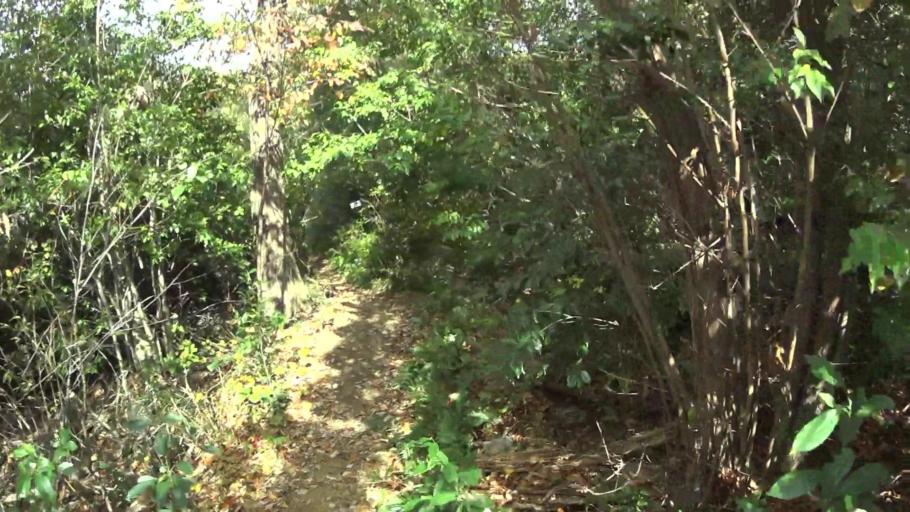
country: JP
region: Kyoto
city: Uji
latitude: 34.9506
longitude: 135.7929
